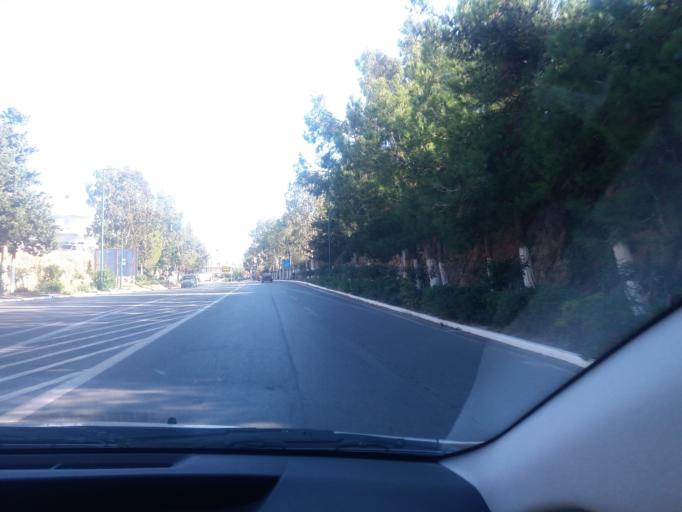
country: GR
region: Crete
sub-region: Nomos Lasithiou
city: Agios Nikolaos
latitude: 35.1991
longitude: 25.7073
